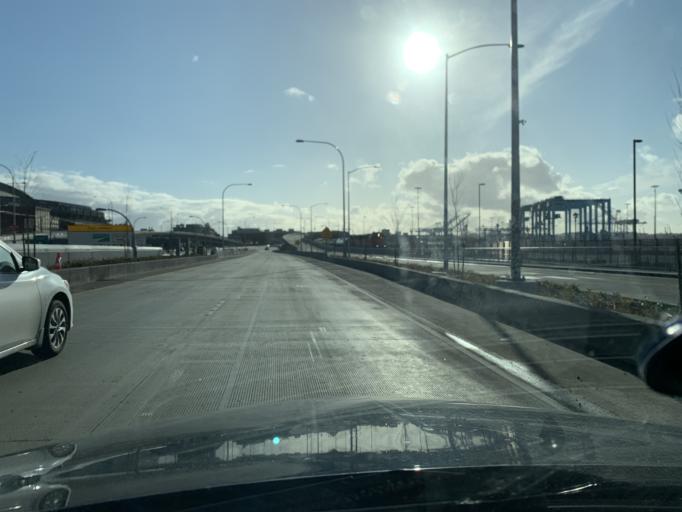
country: US
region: Washington
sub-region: King County
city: Seattle
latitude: 47.5961
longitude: -122.3358
